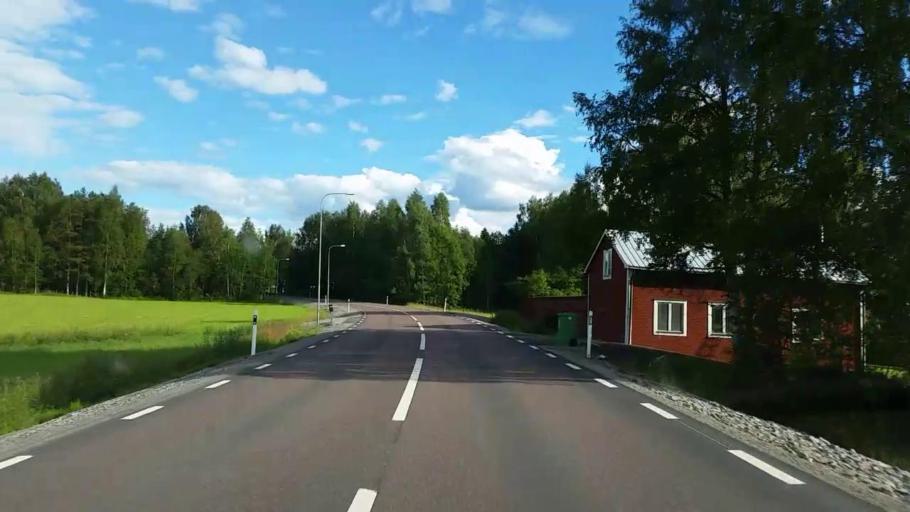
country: SE
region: Gaevleborg
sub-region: Ljusdals Kommun
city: Ljusdal
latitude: 61.8392
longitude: 16.0021
